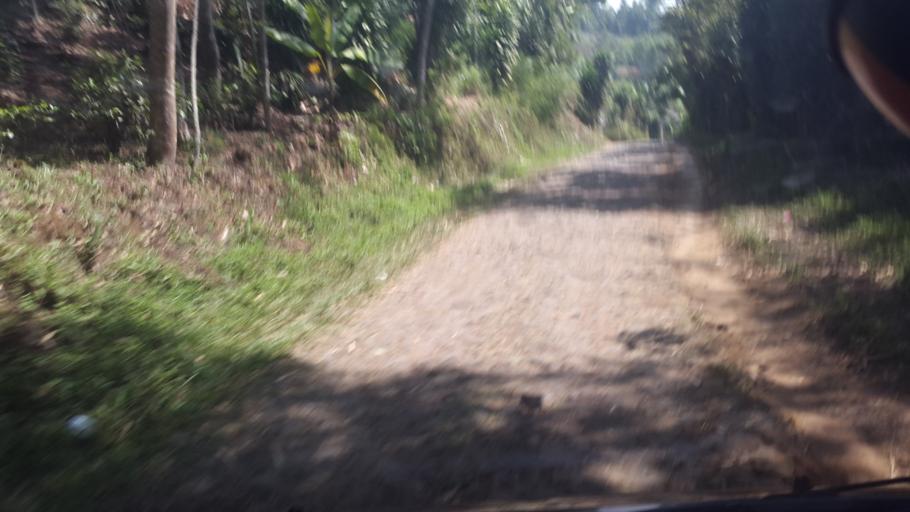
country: ID
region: West Java
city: Pasirhuni
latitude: -7.0284
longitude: 106.9911
